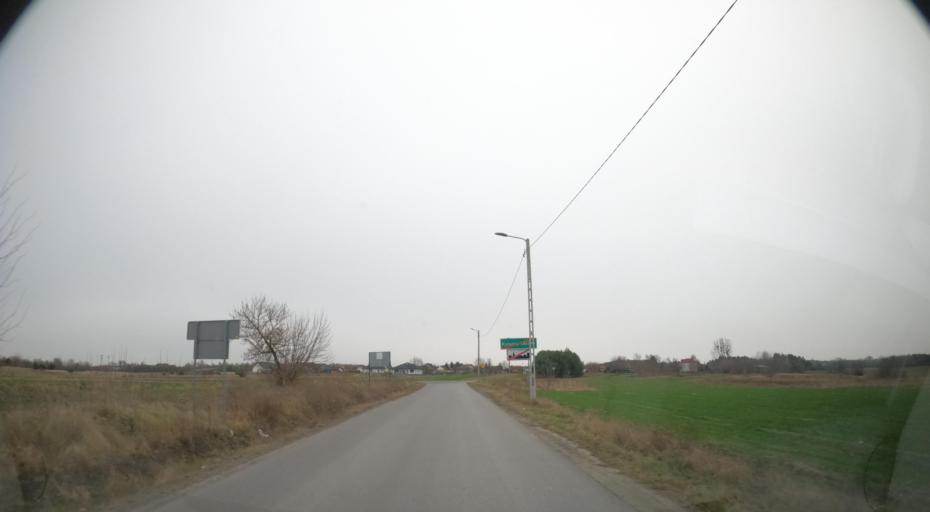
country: PL
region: Masovian Voivodeship
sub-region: Powiat radomski
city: Jastrzebia
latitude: 51.4726
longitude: 21.1997
